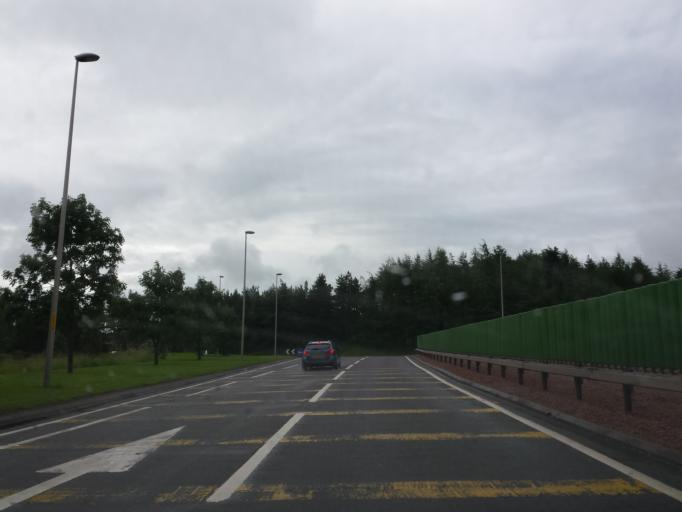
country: GB
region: Scotland
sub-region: Perth and Kinross
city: Perth
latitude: 56.3895
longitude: -3.4875
